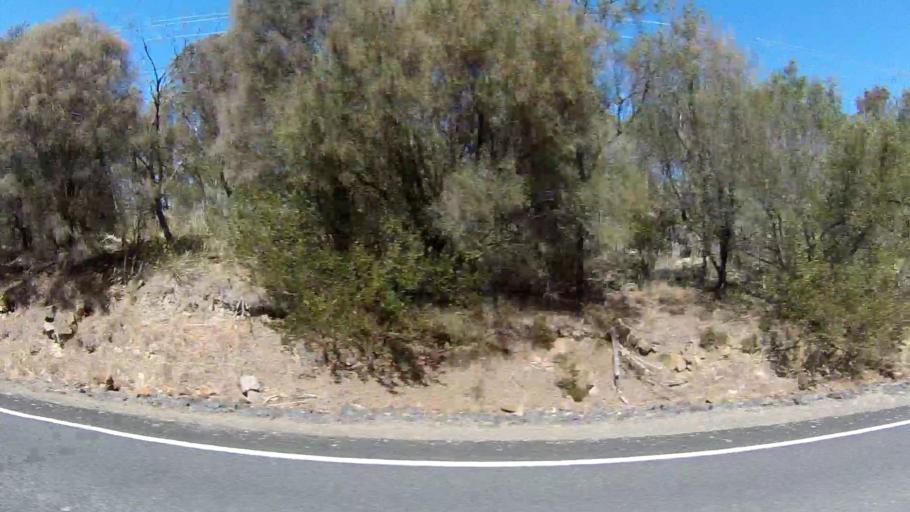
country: AU
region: Tasmania
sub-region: Sorell
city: Sorell
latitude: -42.5844
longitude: 147.8065
